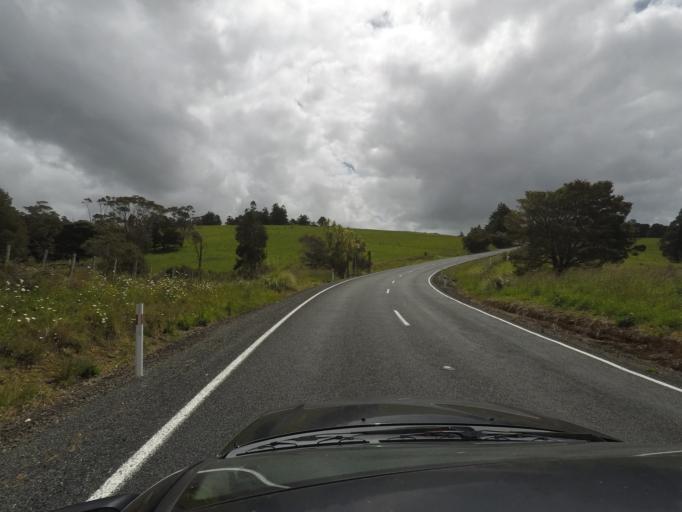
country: NZ
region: Auckland
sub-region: Auckland
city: Parakai
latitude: -36.5044
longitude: 174.5073
